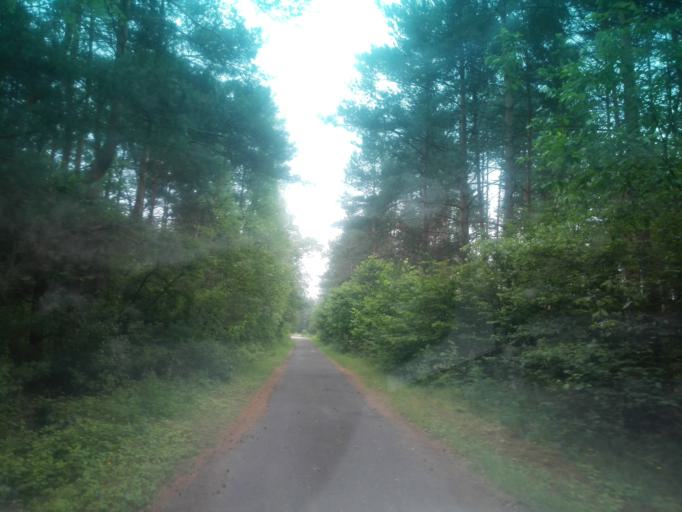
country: PL
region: Silesian Voivodeship
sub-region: Powiat czestochowski
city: Olsztyn
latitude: 50.7460
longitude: 19.2943
